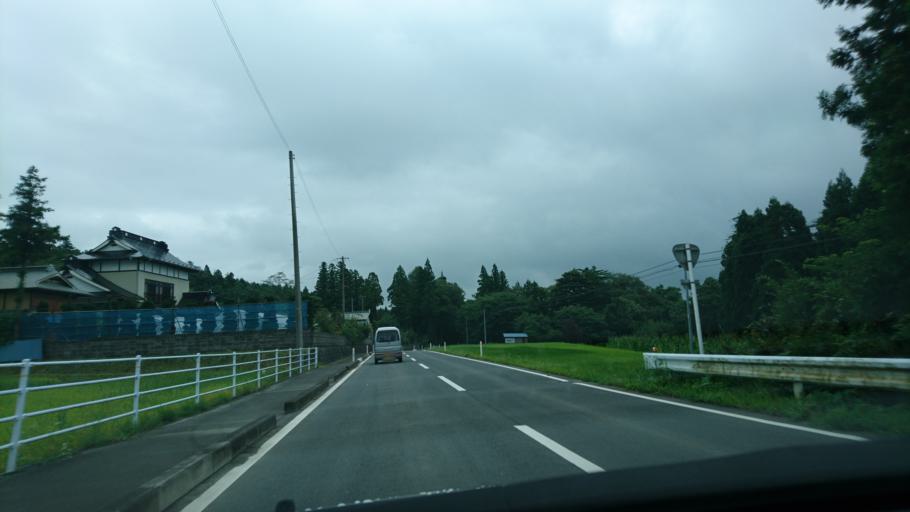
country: JP
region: Iwate
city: Ichinoseki
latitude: 38.8064
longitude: 140.9290
